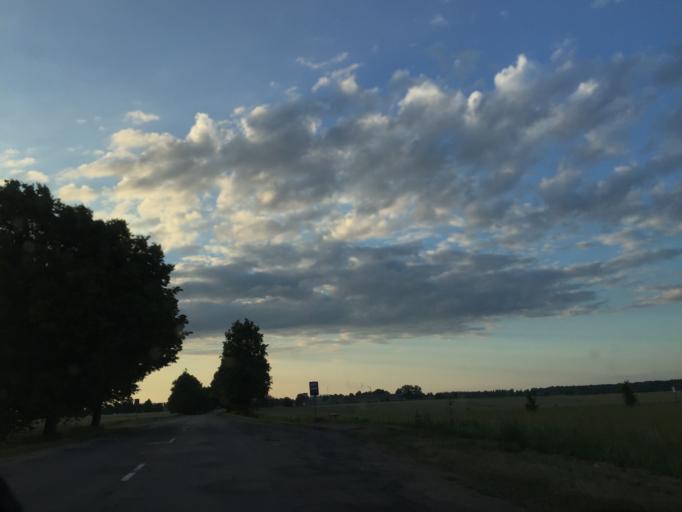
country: LV
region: Sigulda
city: Sigulda
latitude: 57.1318
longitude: 24.8969
